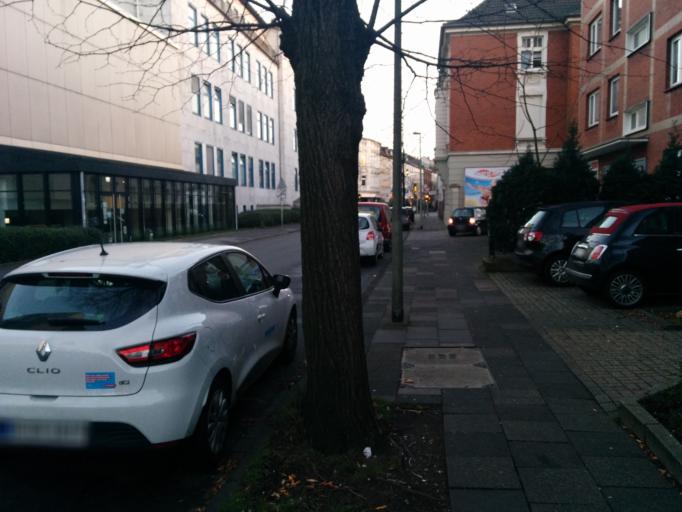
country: DE
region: North Rhine-Westphalia
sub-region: Regierungsbezirk Dusseldorf
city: Duisburg
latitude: 51.4288
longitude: 6.7847
